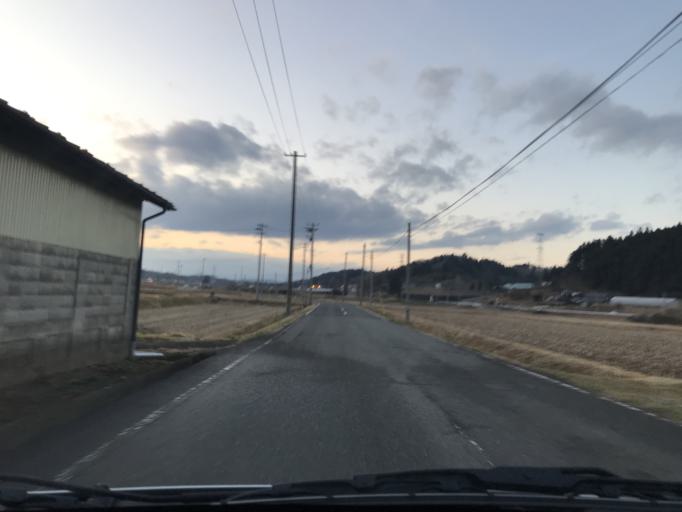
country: JP
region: Iwate
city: Ichinoseki
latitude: 38.8487
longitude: 141.1027
